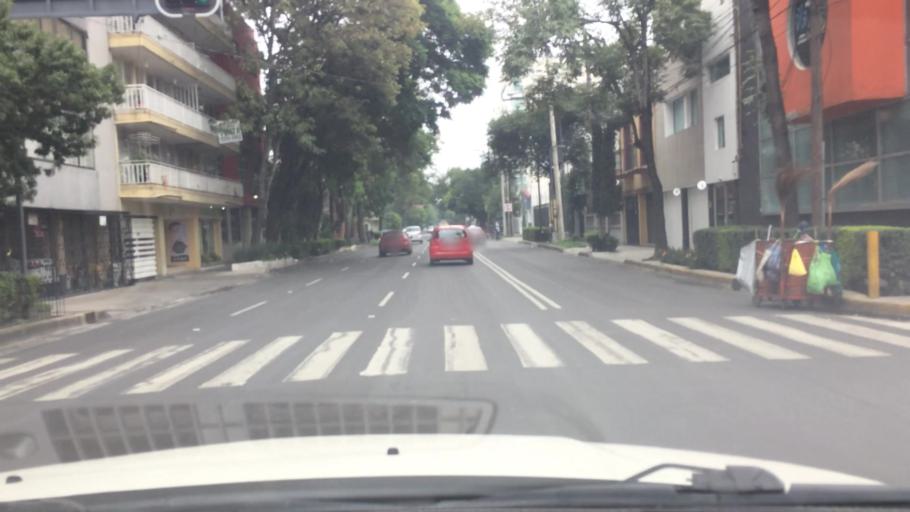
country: MX
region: Mexico City
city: Colonia del Valle
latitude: 19.3777
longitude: -99.1695
